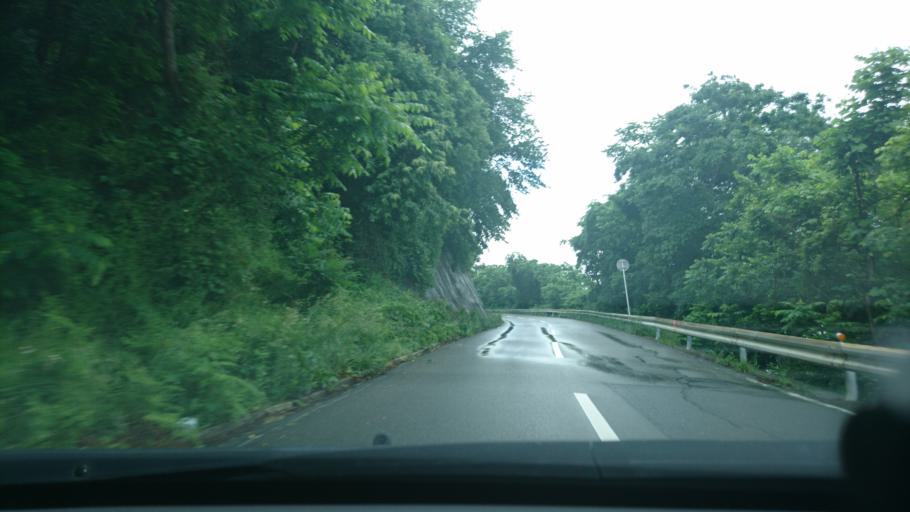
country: JP
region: Miyagi
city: Wakuya
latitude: 38.6832
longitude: 141.2844
